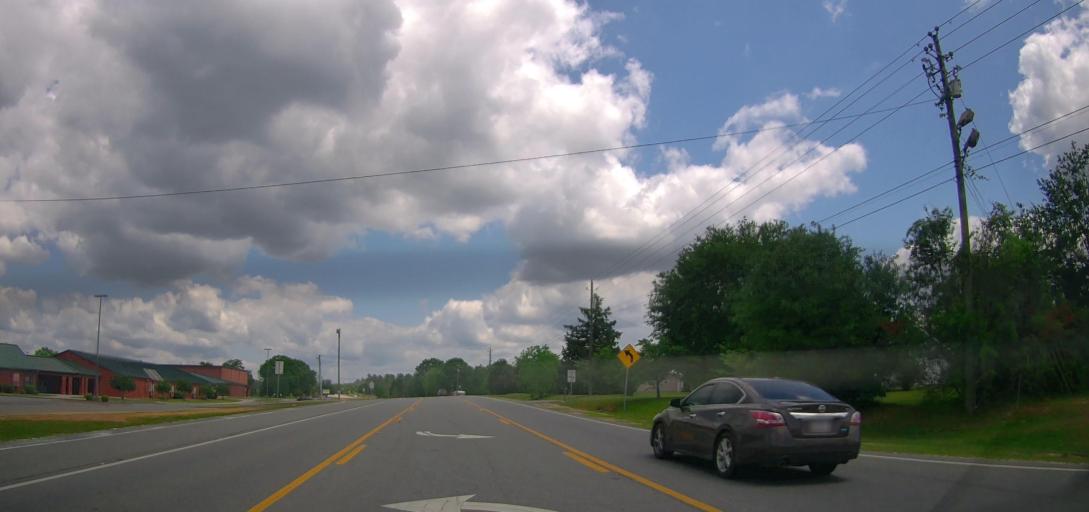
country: US
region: Georgia
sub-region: Laurens County
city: East Dublin
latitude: 32.5608
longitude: -82.8201
